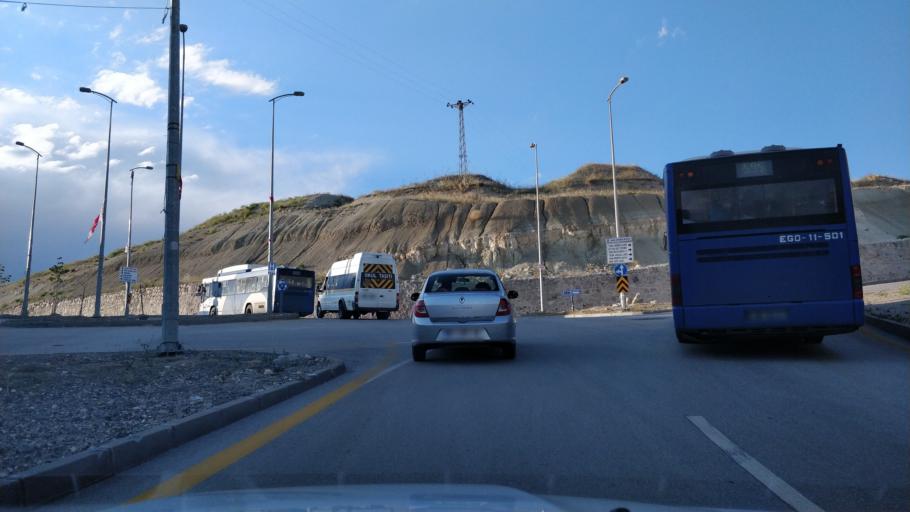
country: TR
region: Ankara
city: Etimesgut
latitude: 39.8314
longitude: 32.5551
